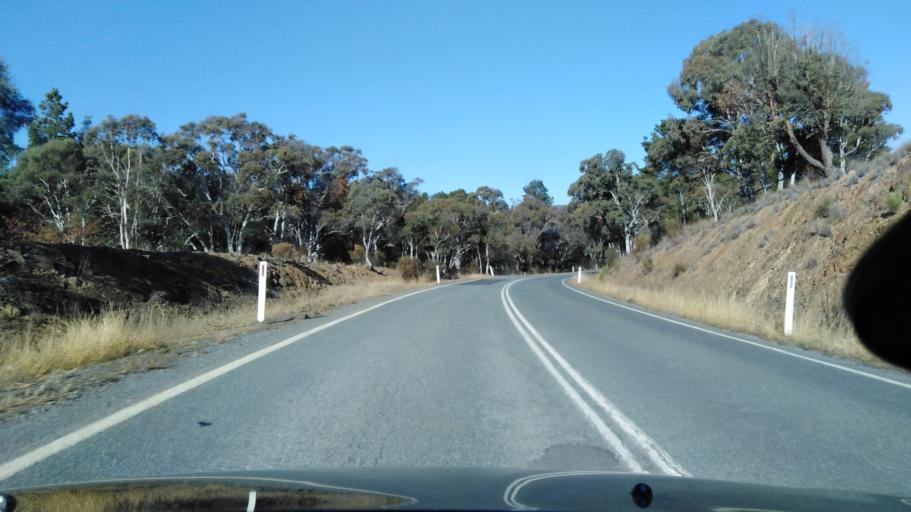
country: AU
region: New South Wales
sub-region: Palerang
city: Bungendore
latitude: -35.1927
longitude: 149.3364
